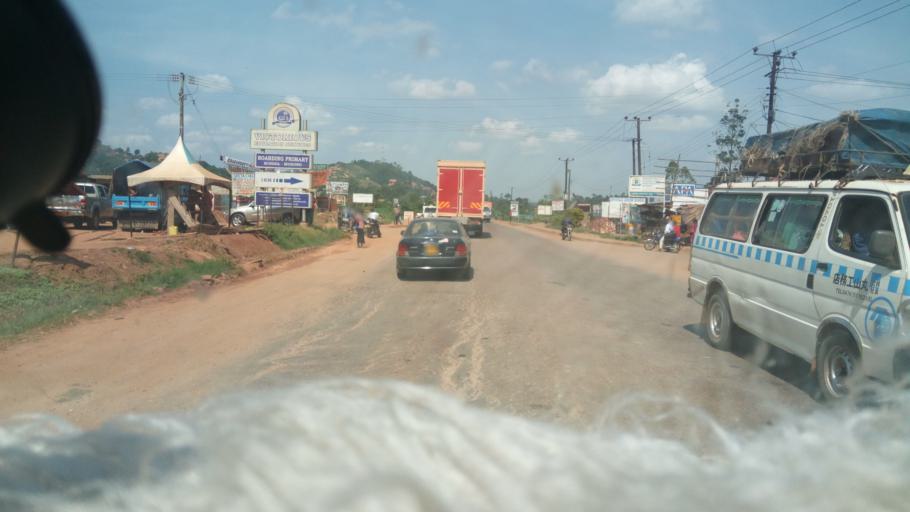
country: UG
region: Central Region
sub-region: Mukono District
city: Mukono
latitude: 0.3656
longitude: 32.8155
